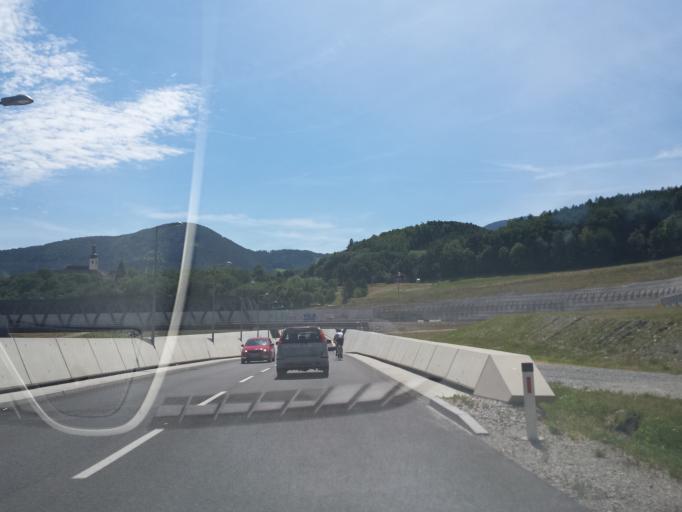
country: AT
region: Lower Austria
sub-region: Politischer Bezirk Neunkirchen
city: Gloggnitz
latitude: 47.6787
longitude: 15.9246
